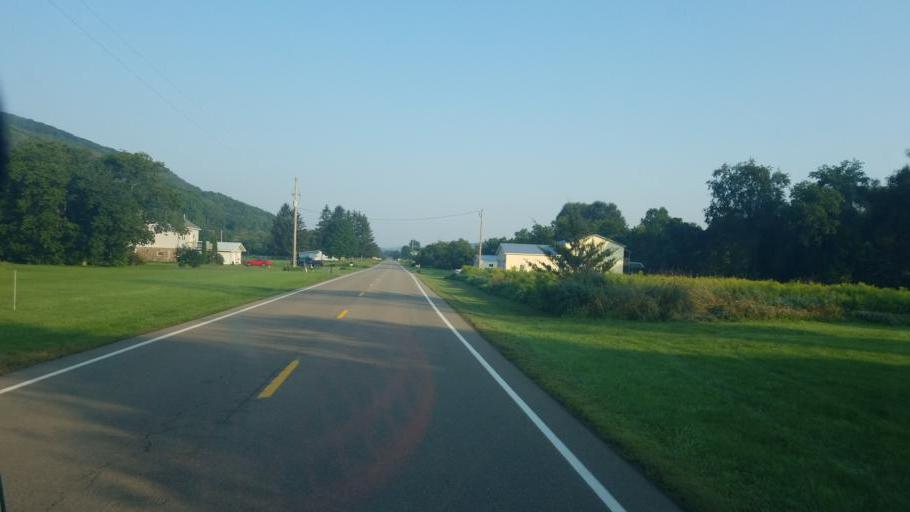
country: US
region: Pennsylvania
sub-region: Tioga County
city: Westfield
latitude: 41.9712
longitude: -77.4569
